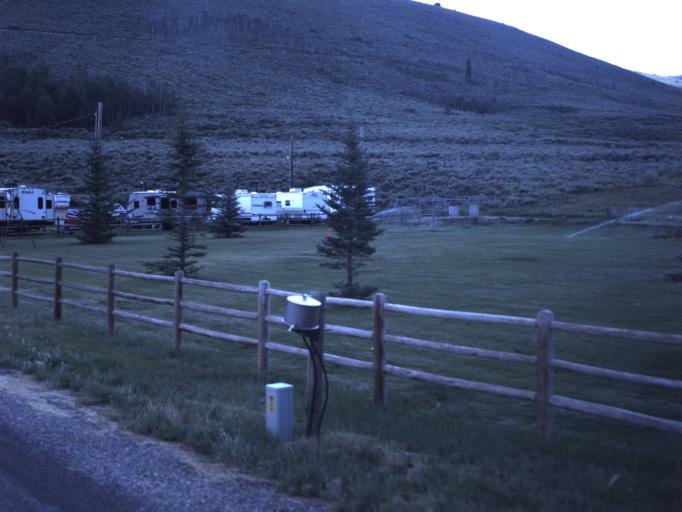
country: US
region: Utah
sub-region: Sanpete County
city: Fairview
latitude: 39.7287
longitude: -111.1580
